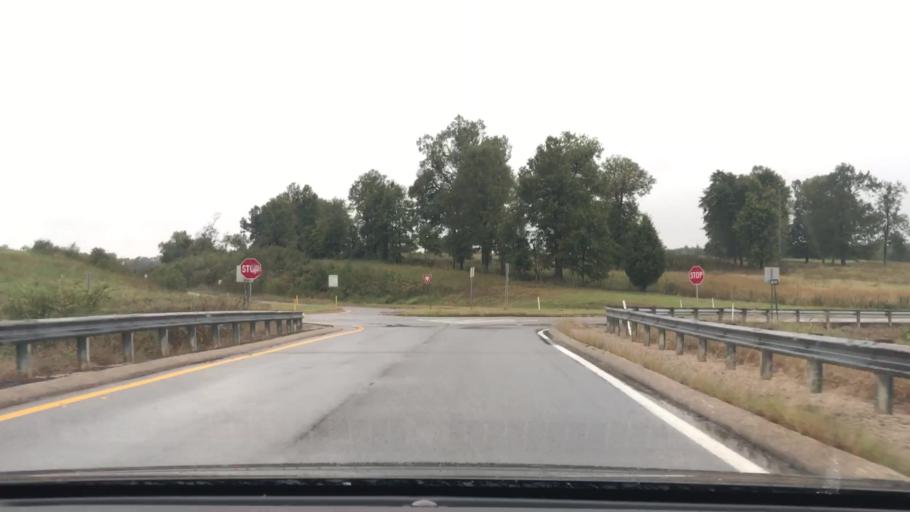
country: US
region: Kentucky
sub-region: Webster County
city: Sebree
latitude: 37.4896
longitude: -87.4744
